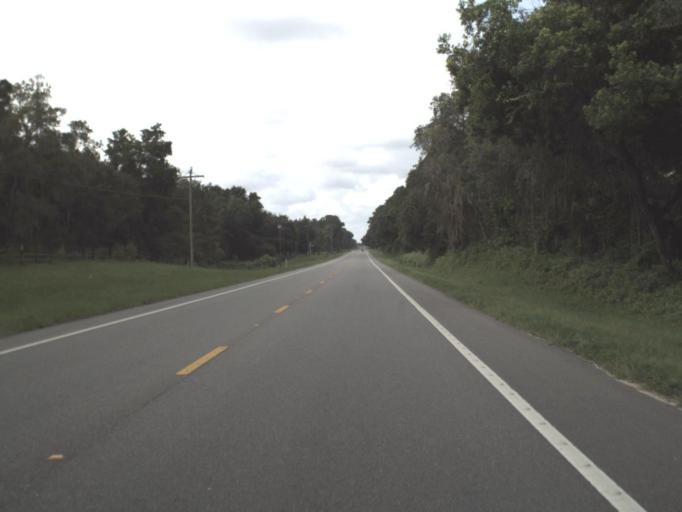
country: US
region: Florida
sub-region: Hernando County
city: Ridge Manor
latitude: 28.5337
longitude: -82.1641
